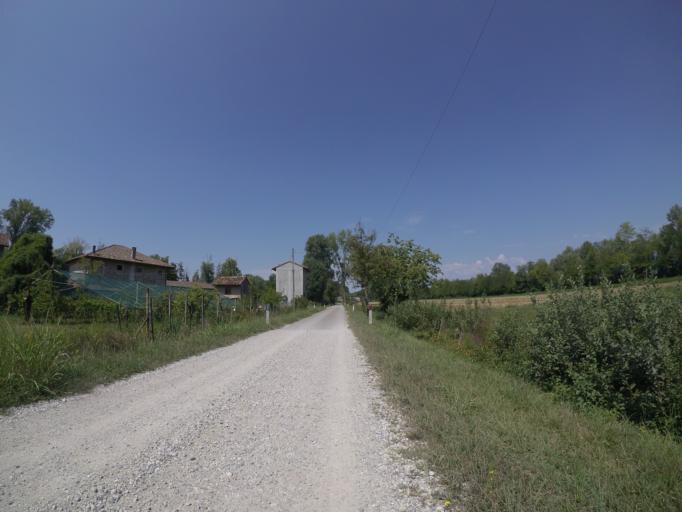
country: IT
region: Friuli Venezia Giulia
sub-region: Provincia di Udine
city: Codroipo
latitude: 45.9395
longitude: 12.9940
